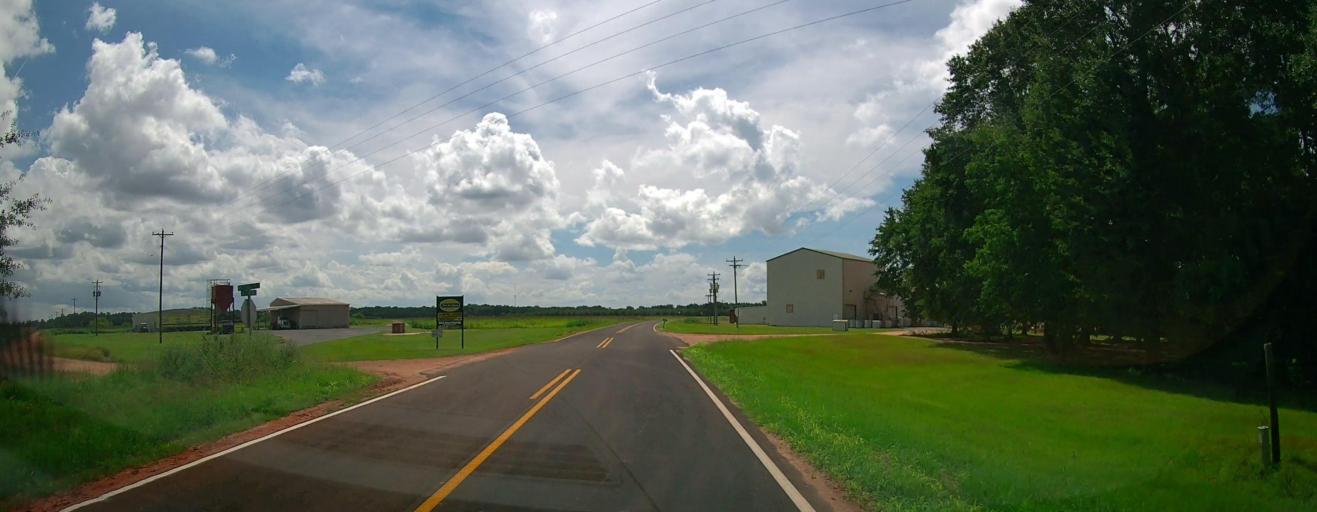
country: US
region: Georgia
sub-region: Macon County
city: Marshallville
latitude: 32.4652
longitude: -83.9035
